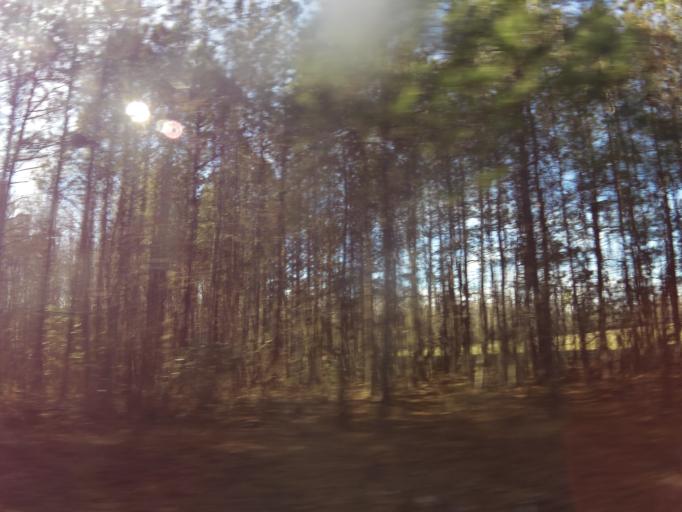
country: US
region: Virginia
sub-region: Isle of Wight County
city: Isle of Wight
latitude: 36.8766
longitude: -76.7289
